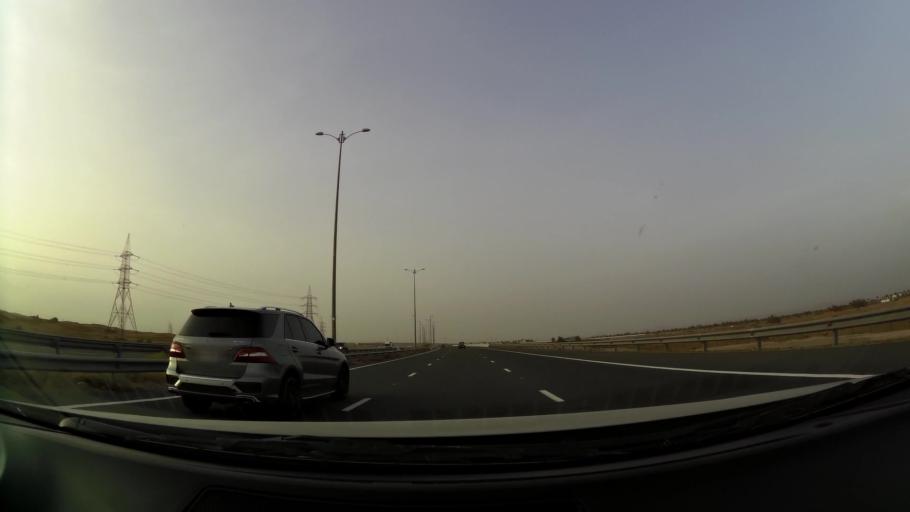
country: OM
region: Al Buraimi
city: Al Buraymi
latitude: 24.3710
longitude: 55.7951
